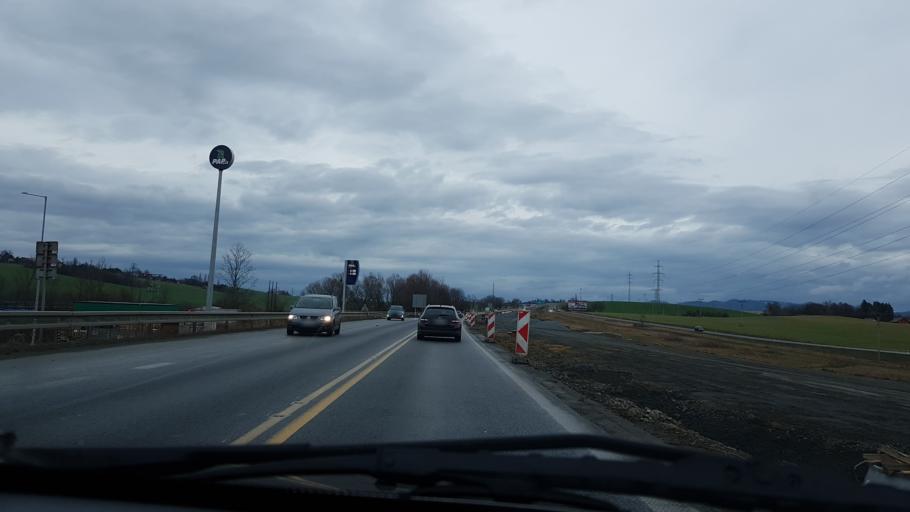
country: CZ
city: Sedlnice
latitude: 49.6369
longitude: 18.1007
